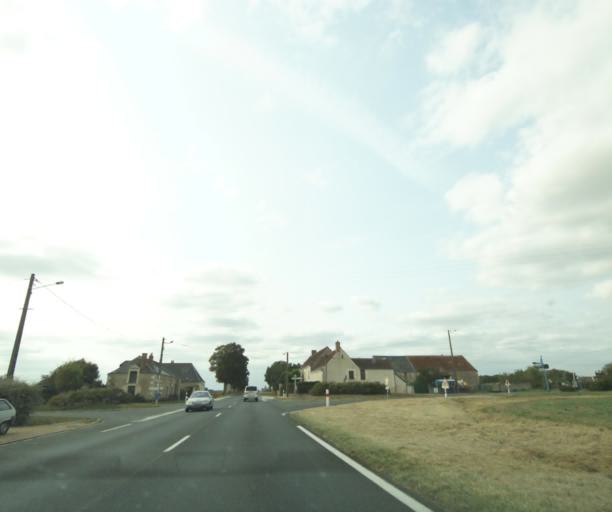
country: FR
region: Centre
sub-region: Departement d'Indre-et-Loire
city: Truyes
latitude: 47.2369
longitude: 0.8676
